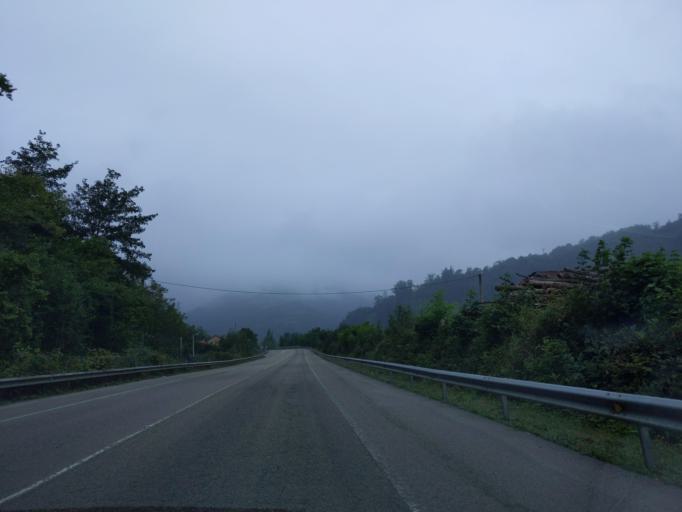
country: ES
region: Asturias
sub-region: Province of Asturias
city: Pola de Laviana
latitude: 43.2358
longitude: -5.5442
